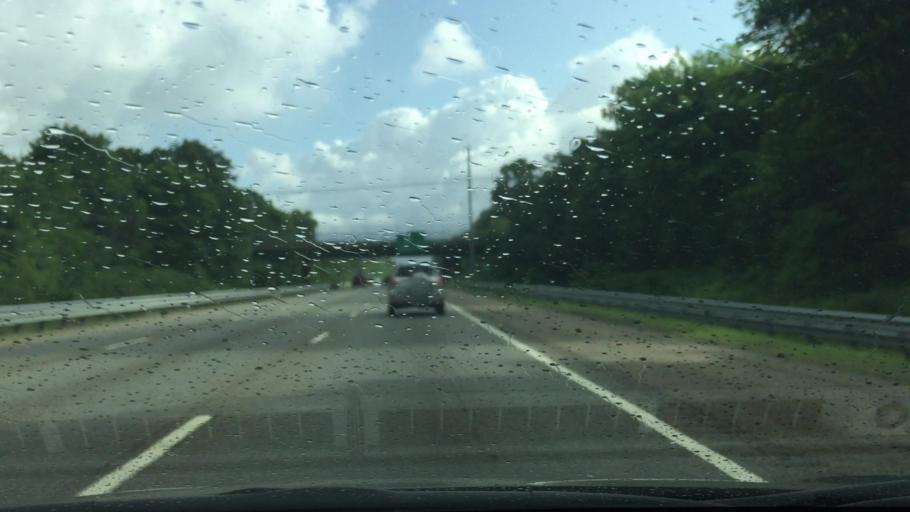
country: US
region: Massachusetts
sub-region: Worcester County
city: Harvard
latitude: 42.4857
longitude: -71.5453
